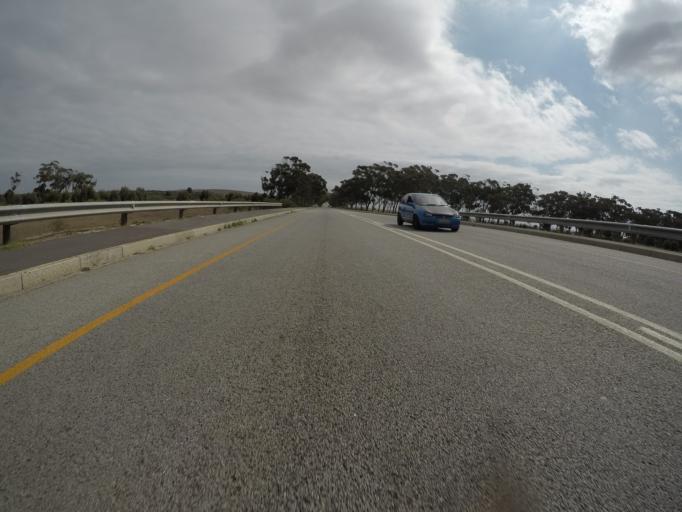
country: ZA
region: Western Cape
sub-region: City of Cape Town
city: Sunset Beach
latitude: -33.7215
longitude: 18.5089
